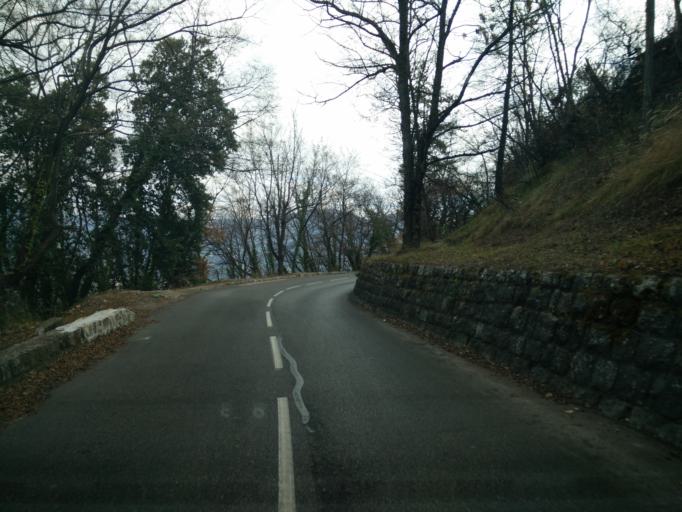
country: FR
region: Provence-Alpes-Cote d'Azur
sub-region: Departement des Alpes-Maritimes
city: Le Broc
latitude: 43.8050
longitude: 7.1693
